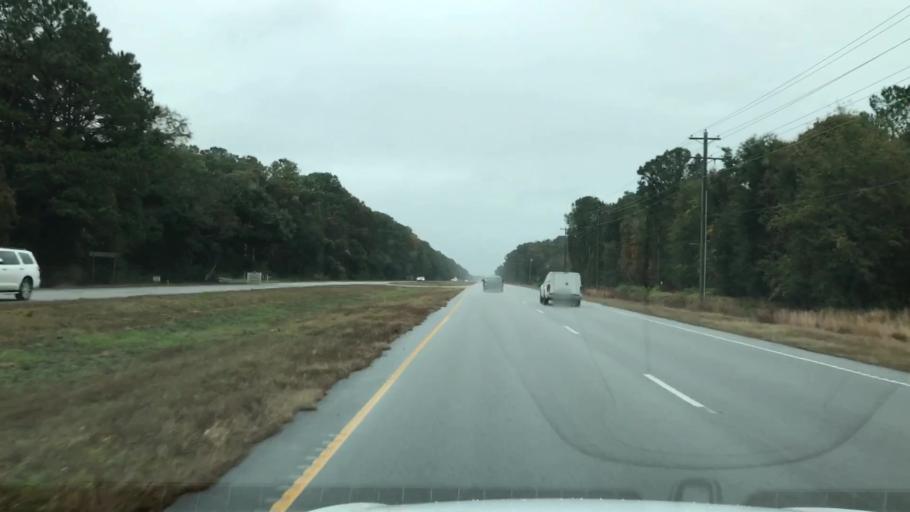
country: US
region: South Carolina
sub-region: Charleston County
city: Isle of Palms
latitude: 32.8995
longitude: -79.7318
